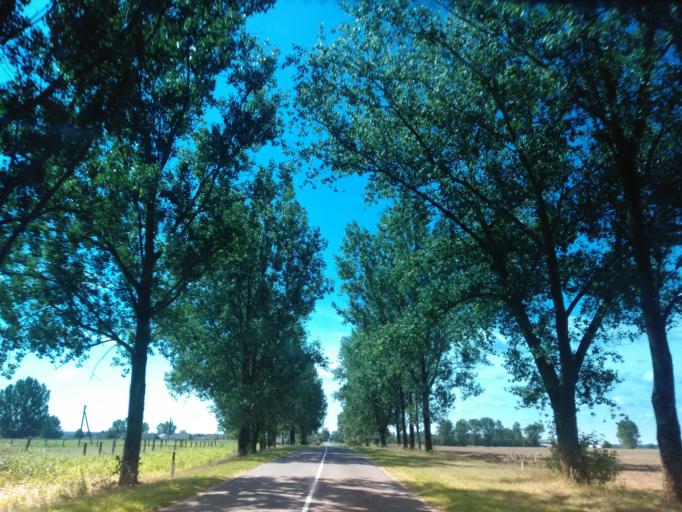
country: BY
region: Minsk
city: Kapyl'
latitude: 53.2635
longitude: 27.1940
